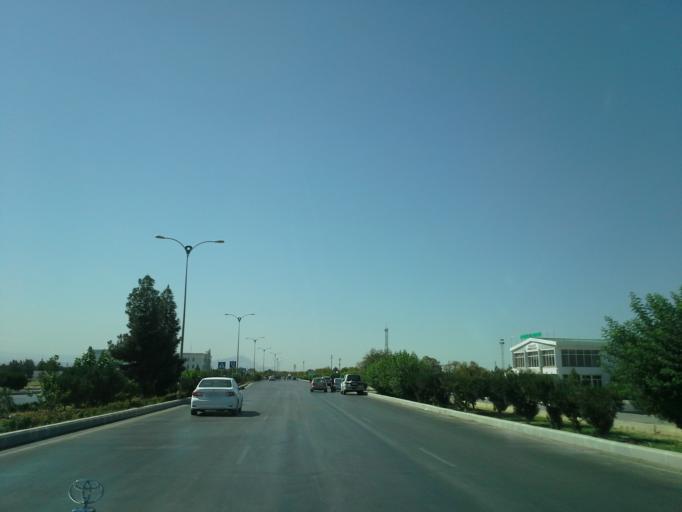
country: TM
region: Ahal
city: Annau
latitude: 37.9092
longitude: 58.5053
